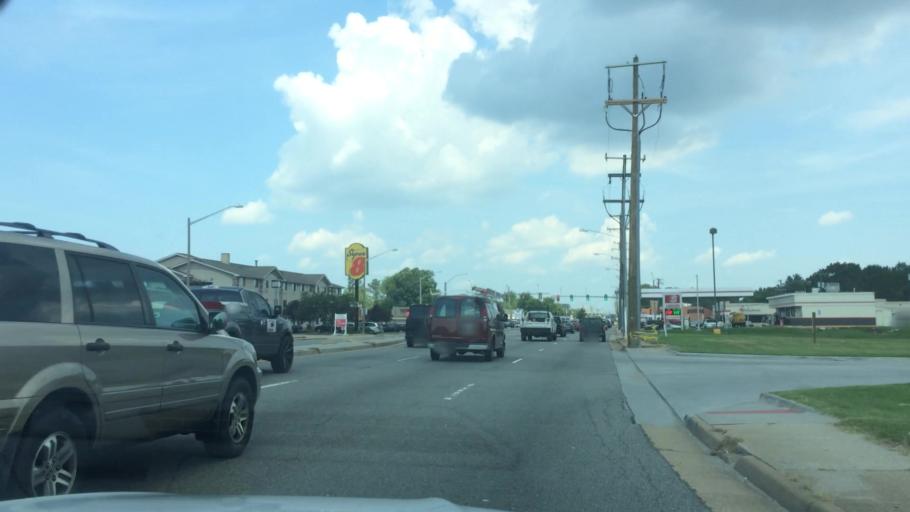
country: US
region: Virginia
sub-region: City of Newport News
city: Newport News
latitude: 37.0205
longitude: -76.4451
